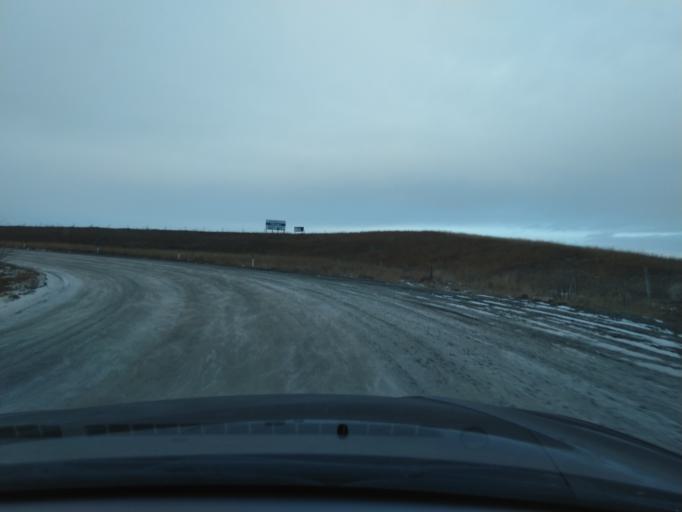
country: CA
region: Alberta
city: Airdrie
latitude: 51.1768
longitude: -114.0207
